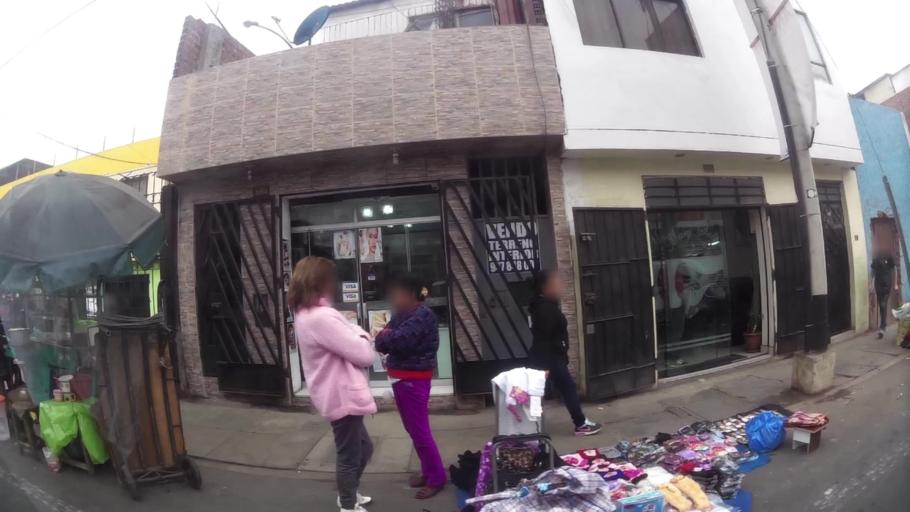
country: PE
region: Lima
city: Lima
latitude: -12.0475
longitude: -77.0190
